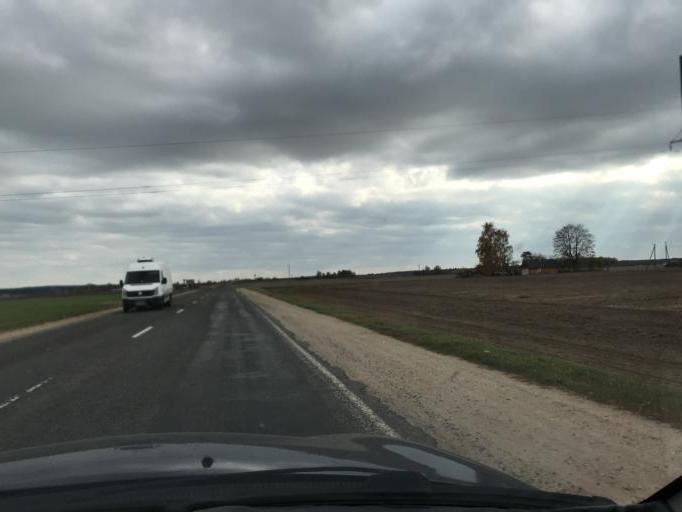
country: BY
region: Grodnenskaya
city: Lida
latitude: 53.8094
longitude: 25.1113
